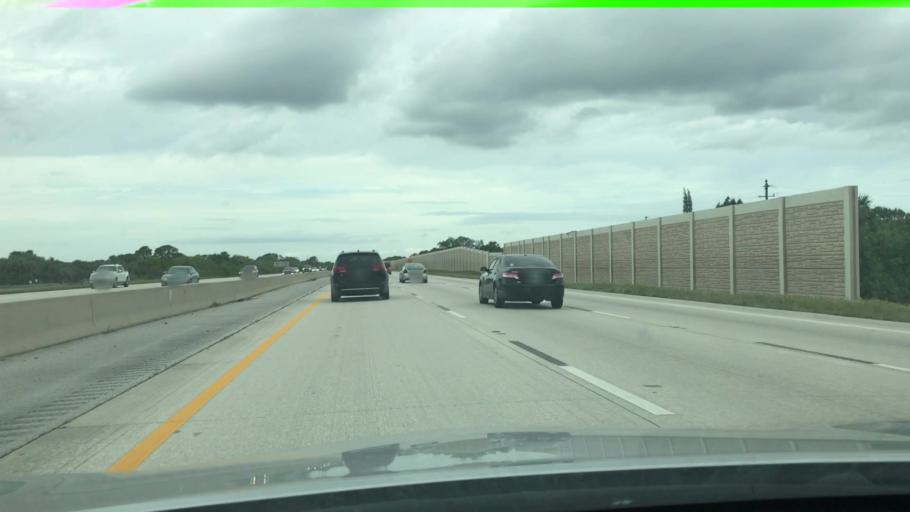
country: US
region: Florida
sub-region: Brevard County
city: Cocoa West
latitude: 28.3445
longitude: -80.7845
